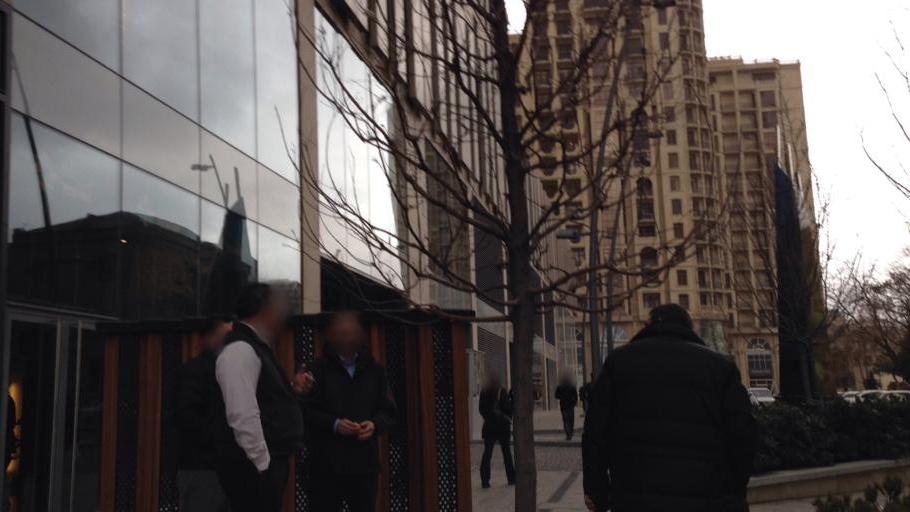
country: AZ
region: Baki
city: Baku
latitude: 40.3759
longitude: 49.8611
